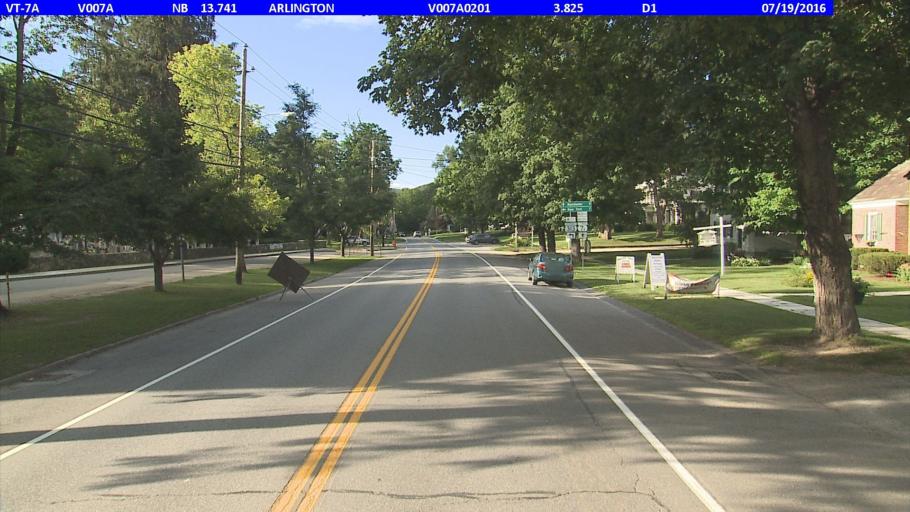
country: US
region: Vermont
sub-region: Bennington County
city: Arlington
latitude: 43.0739
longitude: -73.1543
